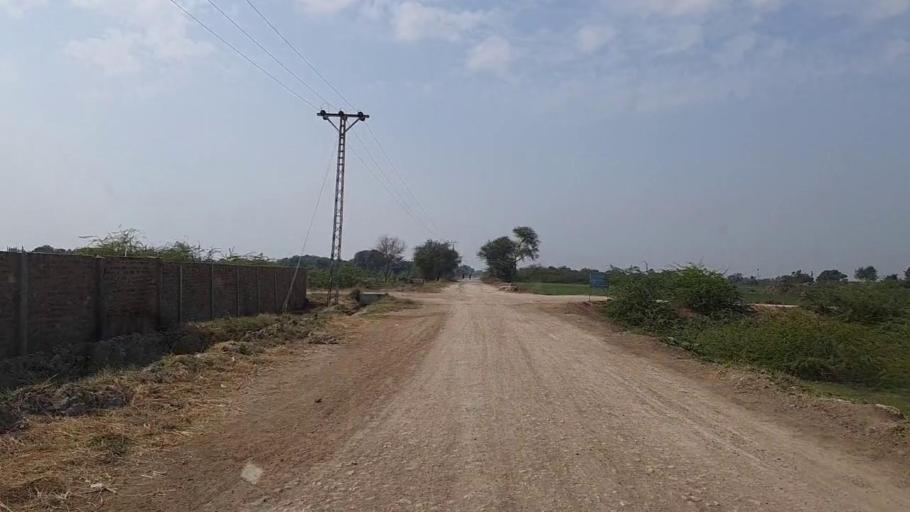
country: PK
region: Sindh
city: Mirwah Gorchani
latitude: 25.3499
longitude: 69.0642
